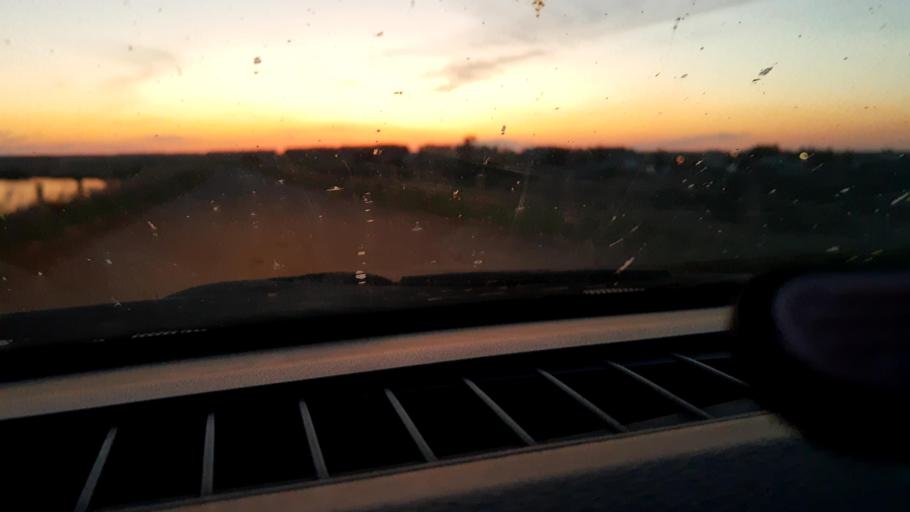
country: RU
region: Bashkortostan
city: Asanovo
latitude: 54.8510
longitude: 55.5902
